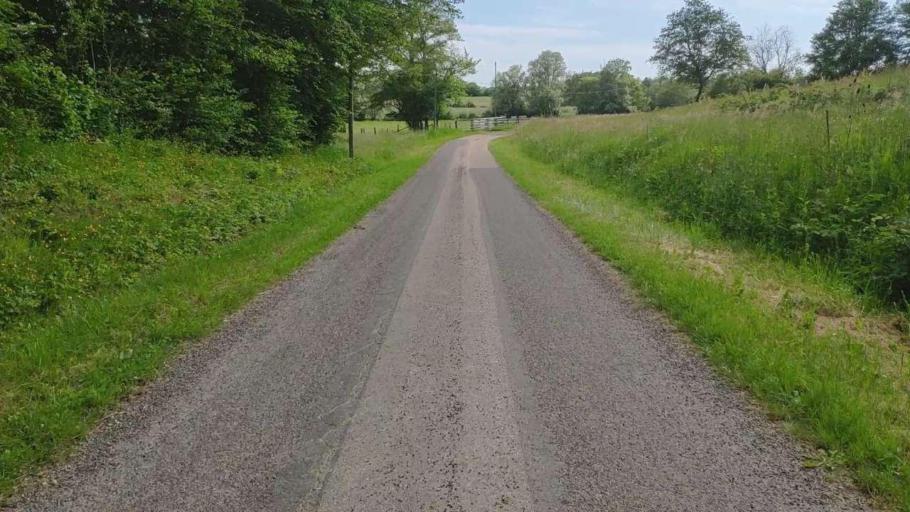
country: FR
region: Bourgogne
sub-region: Departement de Saone-et-Loire
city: Saint-Germain-du-Bois
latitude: 46.8121
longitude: 5.3502
